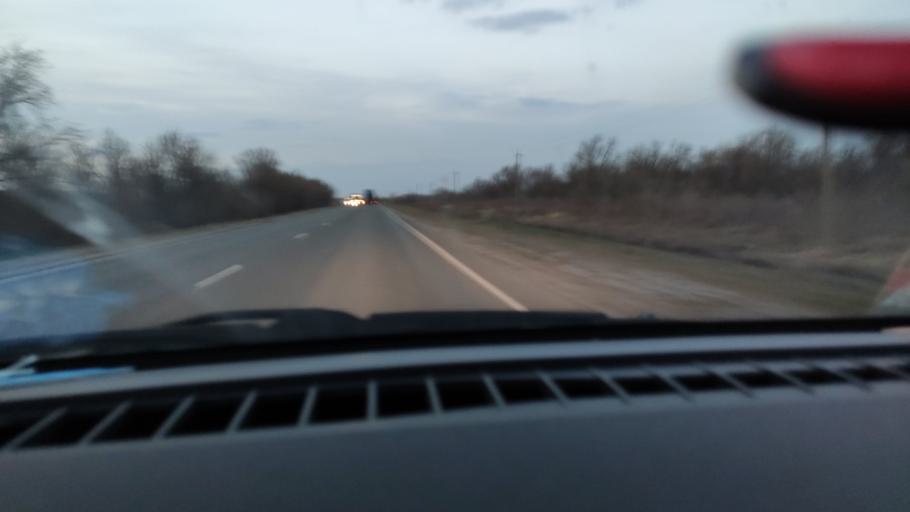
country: RU
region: Saratov
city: Sinodskoye
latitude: 52.0347
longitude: 46.7272
